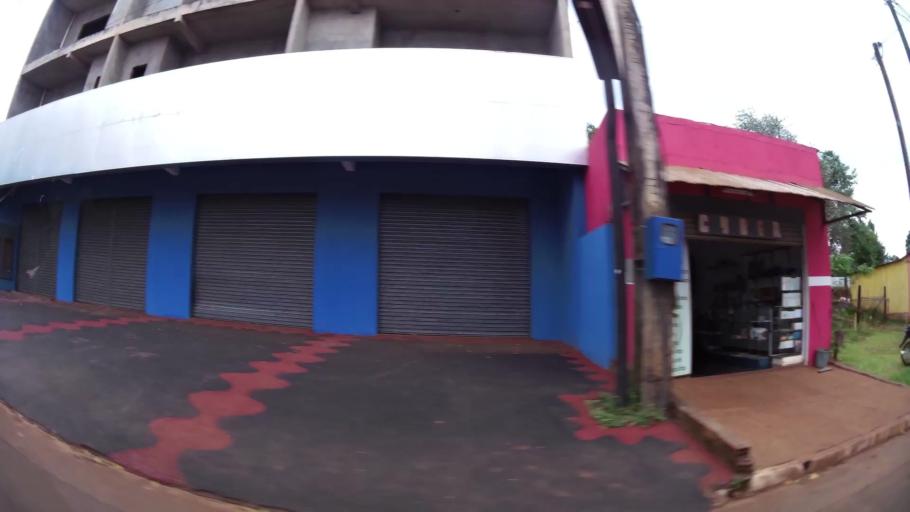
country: PY
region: Alto Parana
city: Presidente Franco
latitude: -25.5251
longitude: -54.6462
